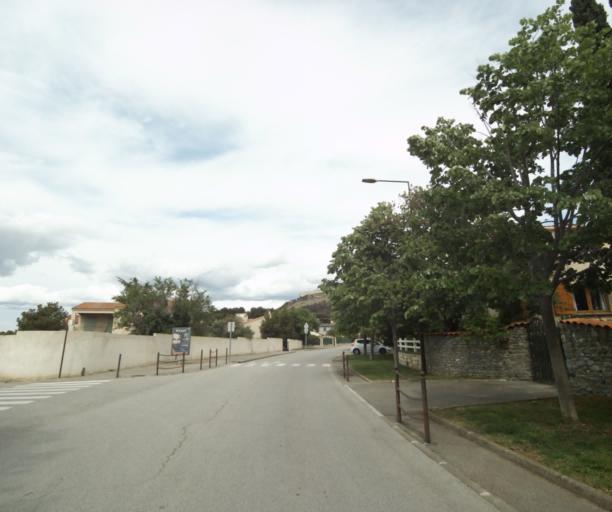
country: FR
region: Provence-Alpes-Cote d'Azur
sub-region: Departement des Bouches-du-Rhone
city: Rognac
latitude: 43.4862
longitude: 5.2374
